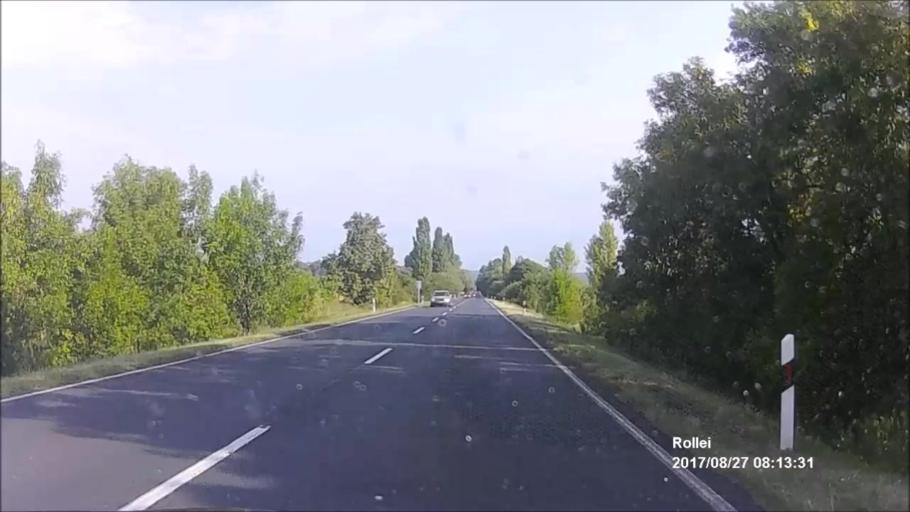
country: HU
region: Veszprem
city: Tapolca
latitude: 46.8461
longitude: 17.3711
